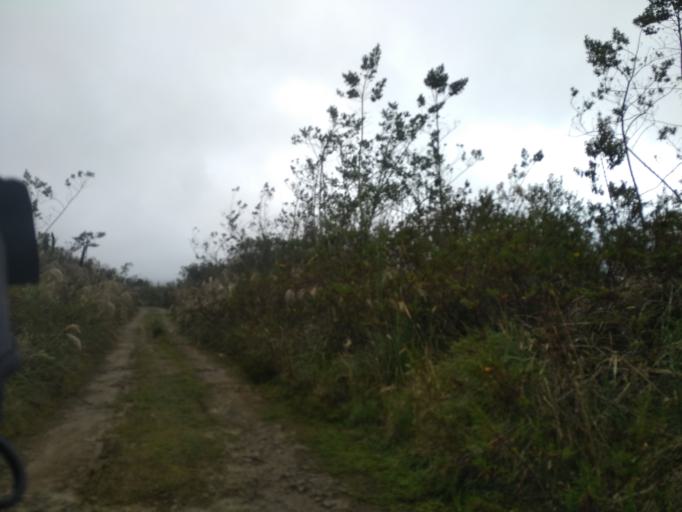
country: EC
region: Carchi
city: San Gabriel
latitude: 0.7065
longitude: -77.8283
